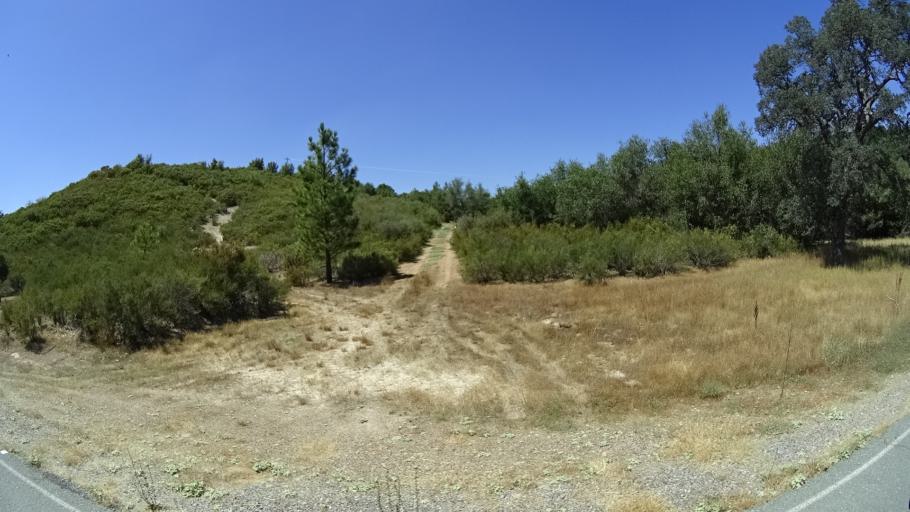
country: US
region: California
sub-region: Calaveras County
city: Mountain Ranch
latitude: 38.2896
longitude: -120.4870
